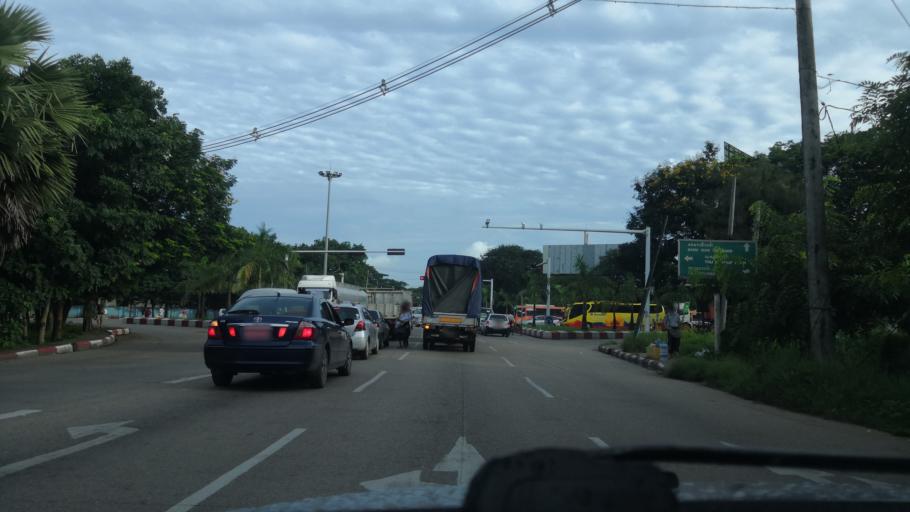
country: MM
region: Yangon
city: Yangon
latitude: 16.8940
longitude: 96.1575
